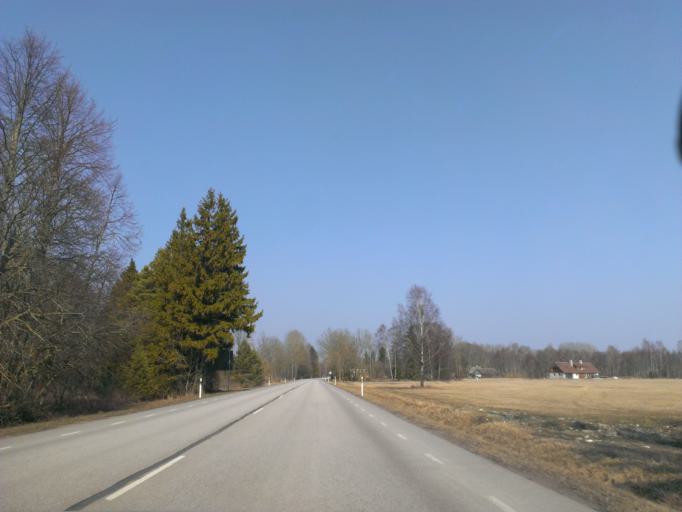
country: EE
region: Saare
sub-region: Orissaare vald
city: Orissaare
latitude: 58.5294
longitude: 23.0391
